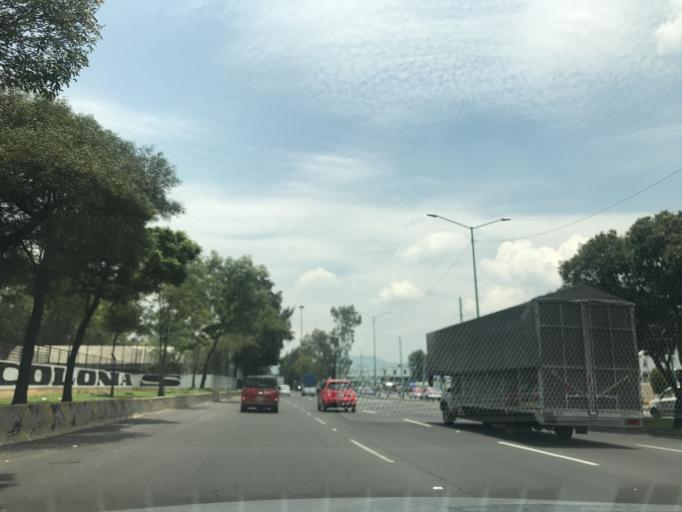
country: MX
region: Mexico
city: Colonia Lindavista
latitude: 19.4777
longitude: -99.1399
